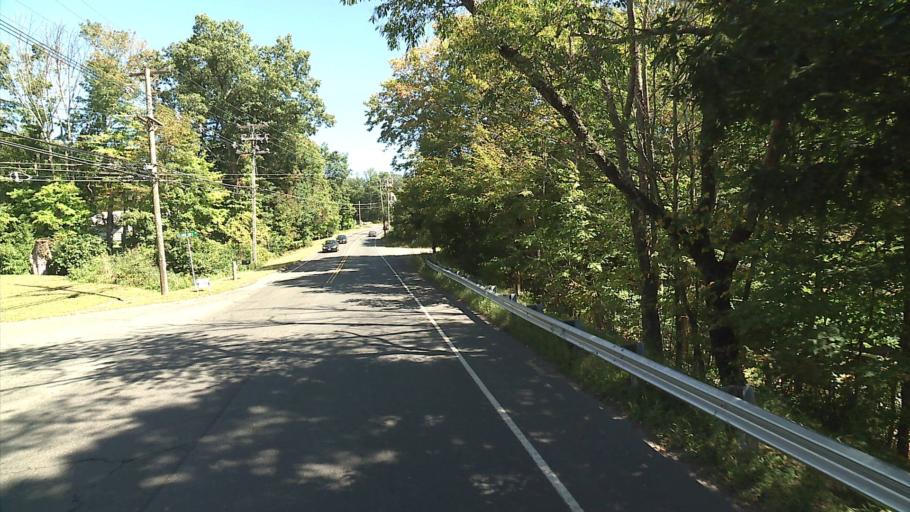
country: US
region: Connecticut
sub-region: New Haven County
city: Prospect
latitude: 41.5056
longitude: -73.0115
